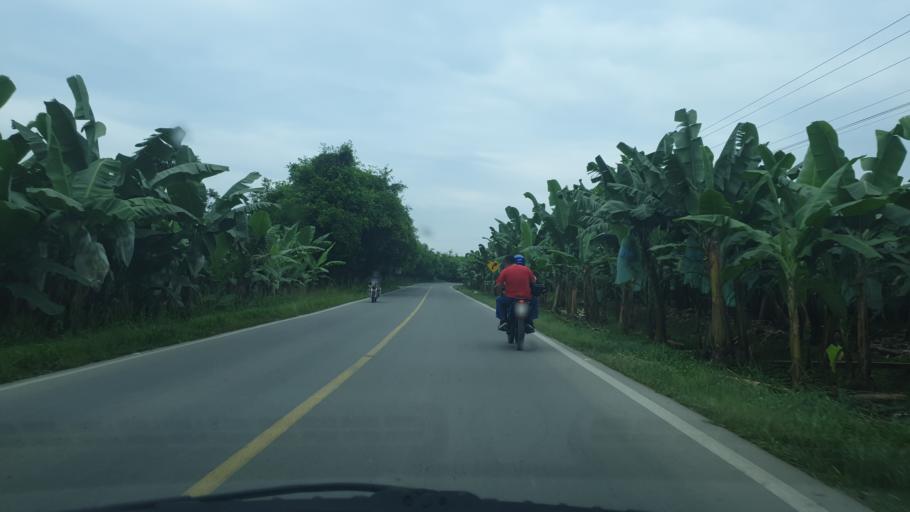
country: EC
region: El Oro
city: Pasaje
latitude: -3.3617
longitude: -79.8379
